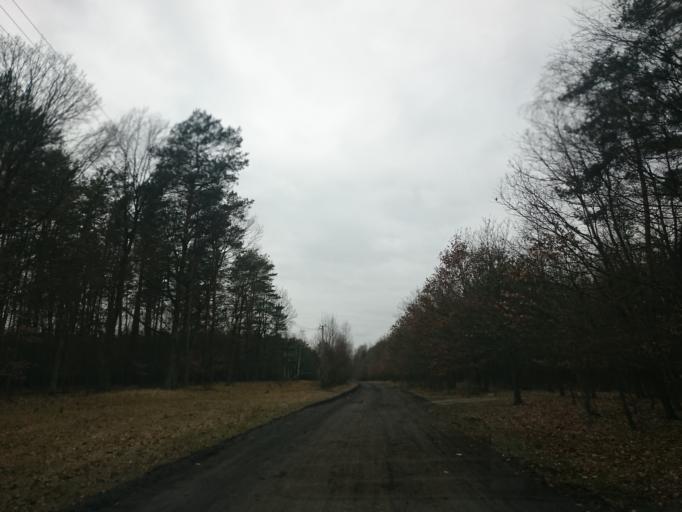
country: PL
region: Kujawsko-Pomorskie
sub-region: Powiat golubsko-dobrzynski
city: Ciechocin
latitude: 53.0757
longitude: 18.9450
